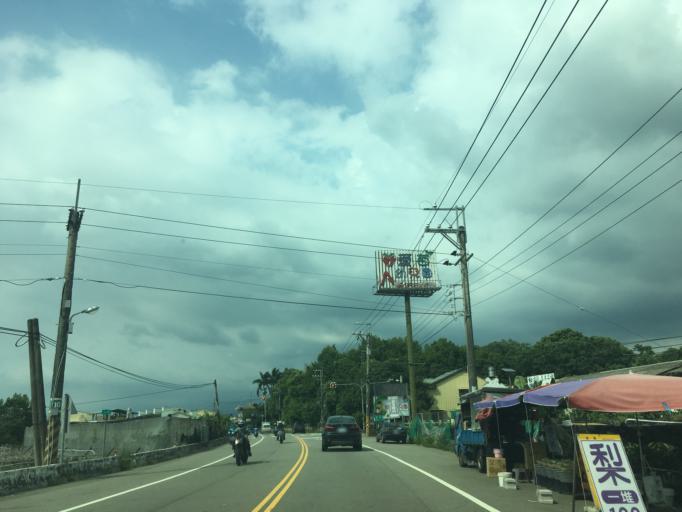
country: TW
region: Taiwan
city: Fengyuan
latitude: 24.2359
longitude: 120.8047
